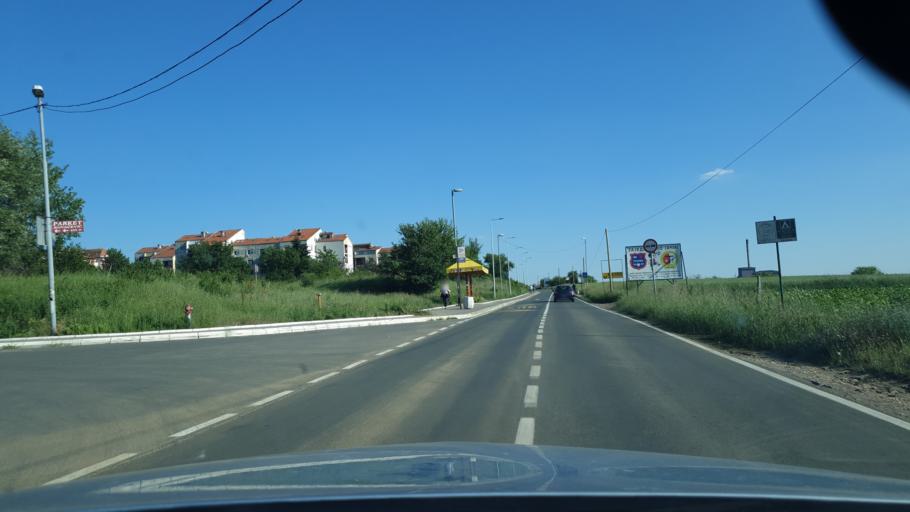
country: RS
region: Central Serbia
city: Sremcica
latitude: 44.6976
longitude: 20.3781
